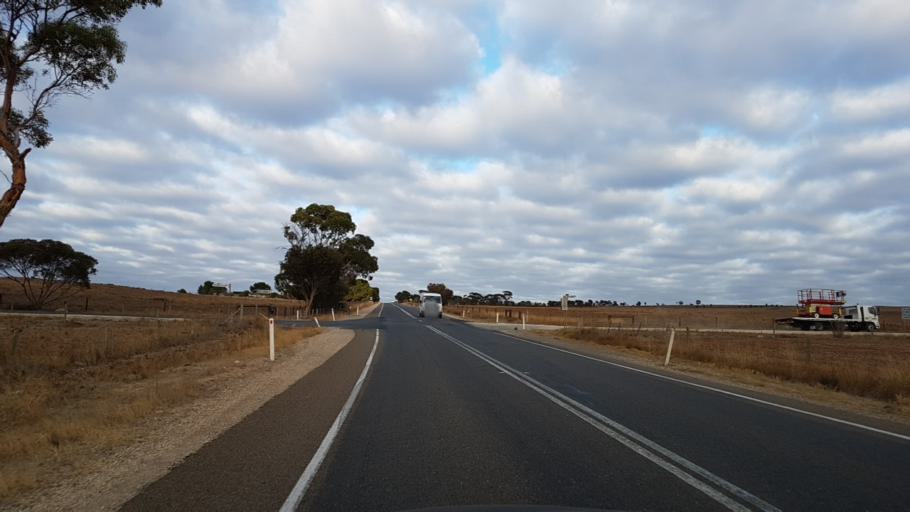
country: AU
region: South Australia
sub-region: Mount Barker
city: Callington
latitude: -35.1830
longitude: 139.0034
